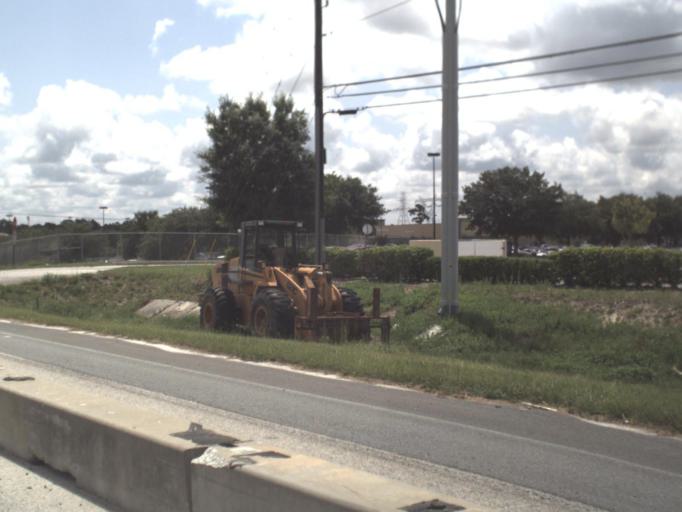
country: US
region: Florida
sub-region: Hernando County
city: High Point
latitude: 28.5336
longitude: -82.5075
